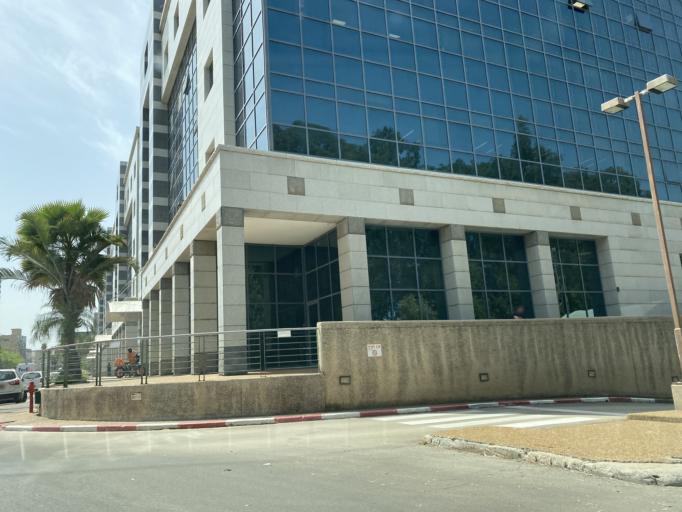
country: IL
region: Tel Aviv
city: Herzliya Pituah
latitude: 32.1679
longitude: 34.8116
